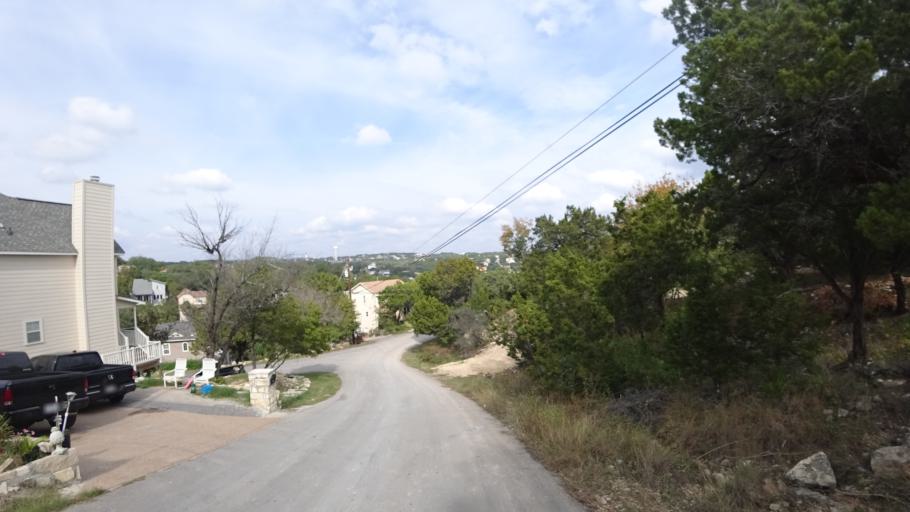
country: US
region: Texas
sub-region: Travis County
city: Hudson Bend
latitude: 30.3783
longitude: -97.9249
